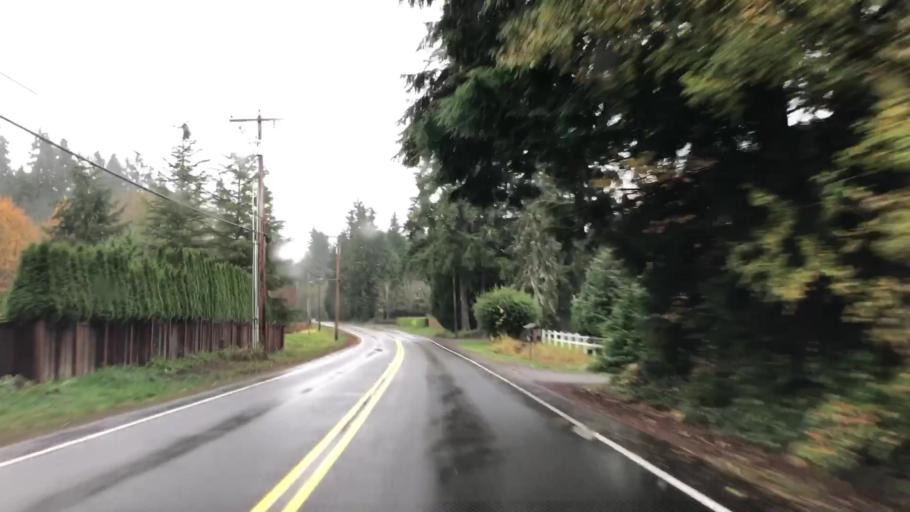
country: US
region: Washington
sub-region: King County
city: Cottage Lake
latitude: 47.7600
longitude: -122.1118
